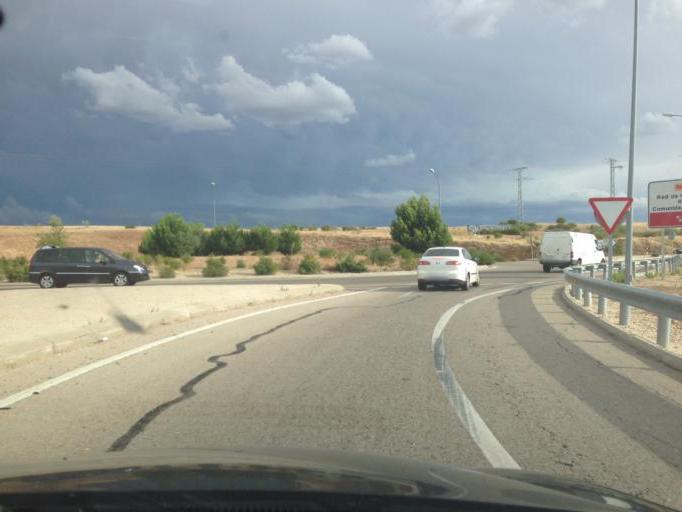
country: ES
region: Madrid
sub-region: Provincia de Madrid
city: Paracuellos de Jarama
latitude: 40.5157
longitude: -3.5045
